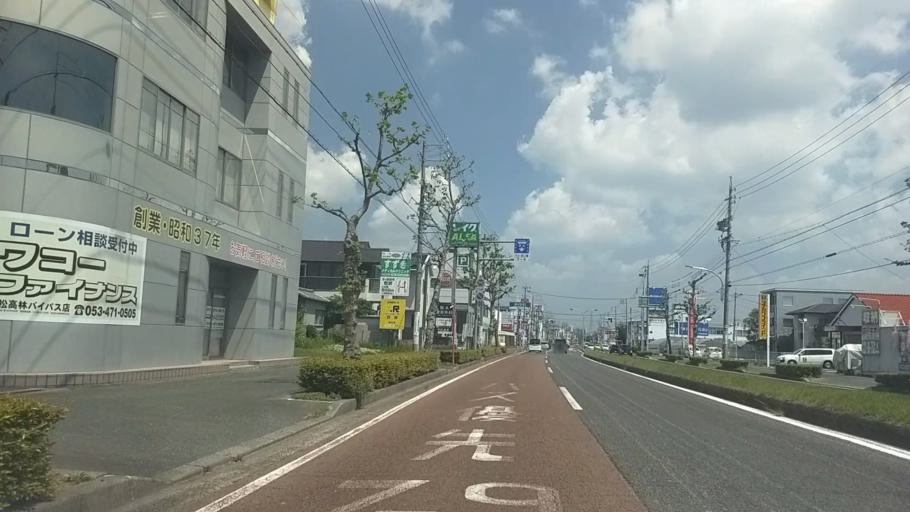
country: JP
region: Shizuoka
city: Hamamatsu
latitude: 34.7257
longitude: 137.7313
